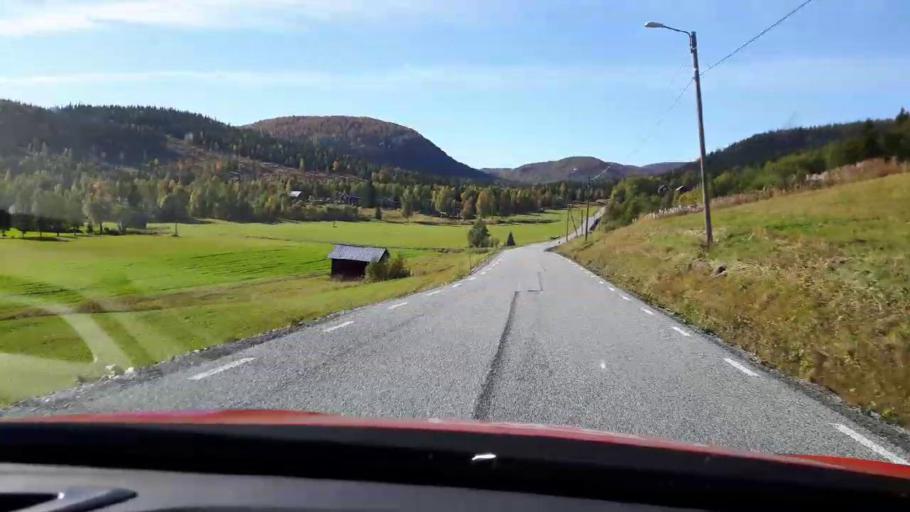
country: NO
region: Nord-Trondelag
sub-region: Royrvik
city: Royrvik
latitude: 64.7286
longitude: 13.9593
